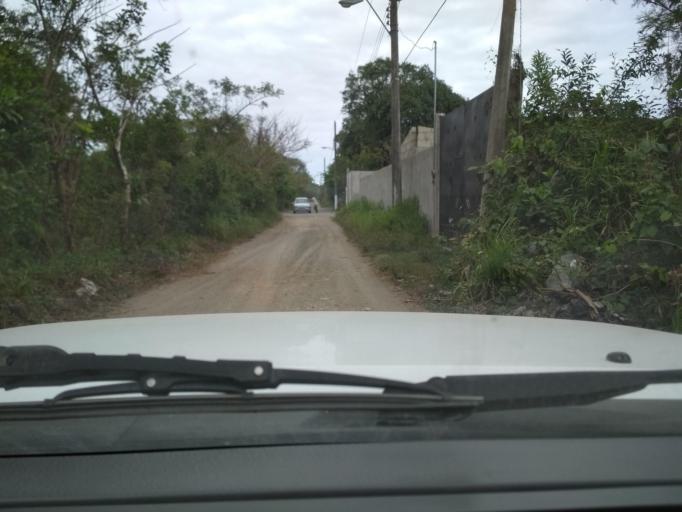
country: MX
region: Veracruz
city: El Tejar
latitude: 19.0705
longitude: -96.1428
